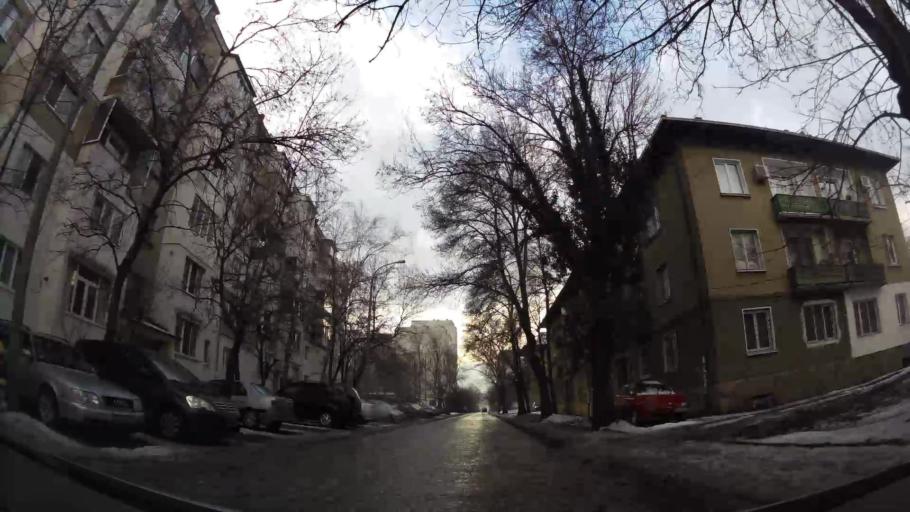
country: BG
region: Sofia-Capital
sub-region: Stolichna Obshtina
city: Sofia
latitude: 42.7005
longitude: 23.2801
